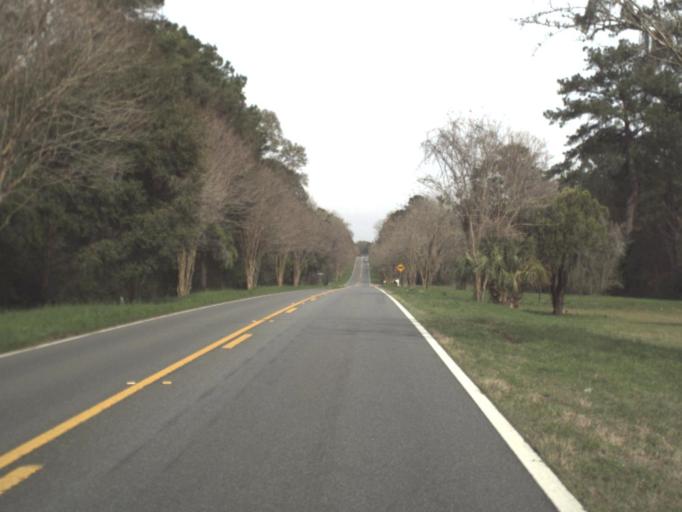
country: US
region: Florida
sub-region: Jefferson County
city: Monticello
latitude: 30.5268
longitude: -84.0056
